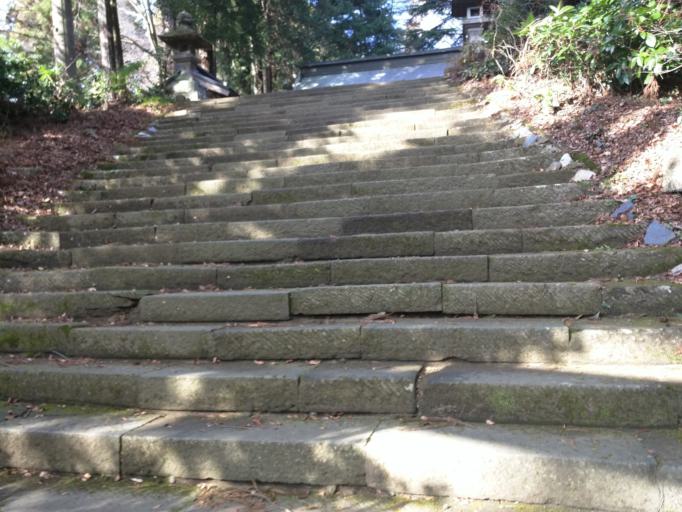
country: JP
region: Fukushima
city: Ishikawa
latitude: 37.0312
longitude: 140.3769
